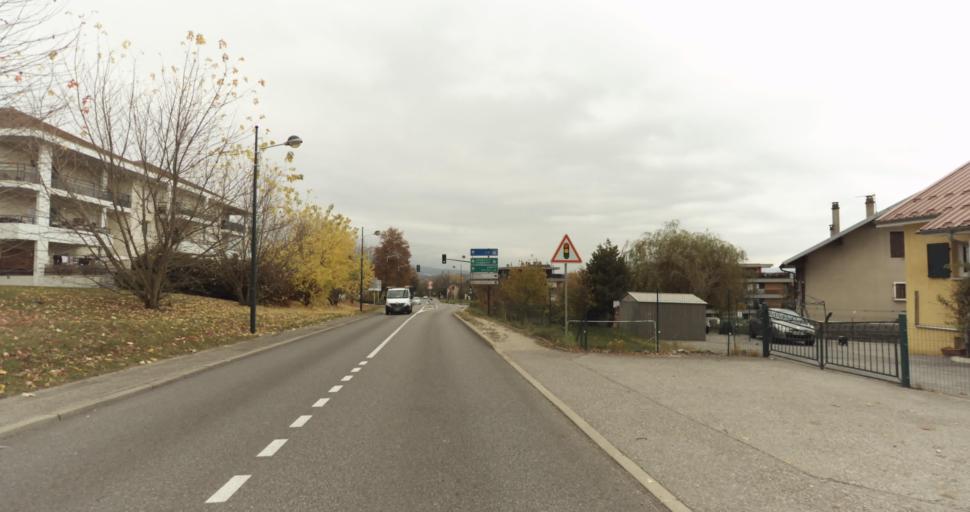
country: FR
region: Rhone-Alpes
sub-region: Departement de la Haute-Savoie
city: Pringy
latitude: 45.9478
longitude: 6.1215
